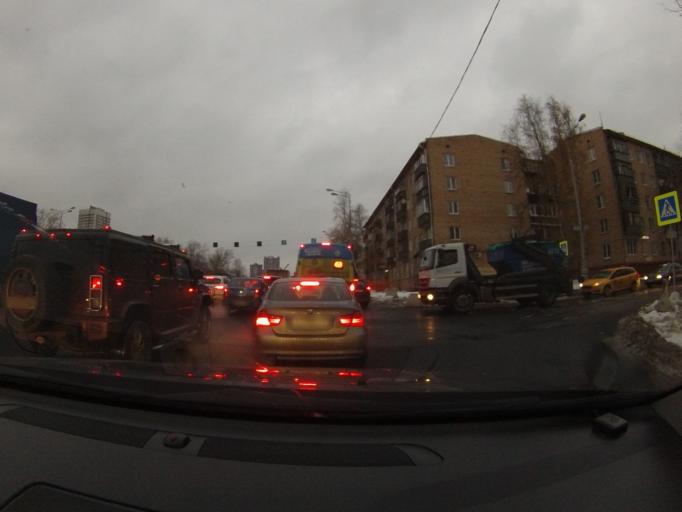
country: RU
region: Moscow
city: Davydkovo
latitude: 55.7154
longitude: 37.4529
